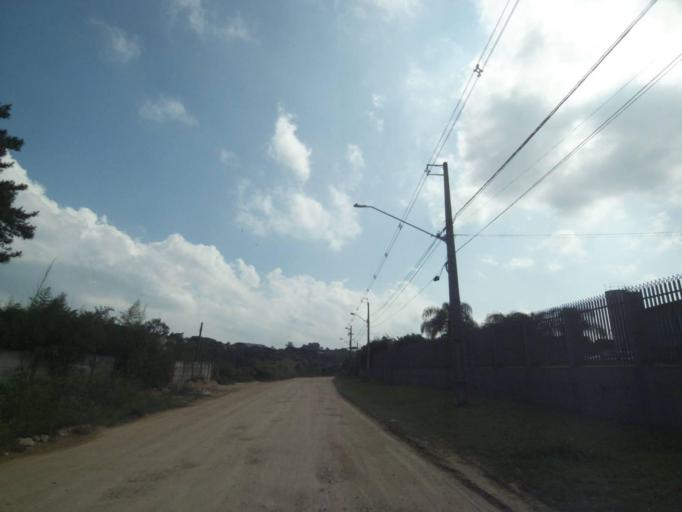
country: BR
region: Parana
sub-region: Araucaria
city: Araucaria
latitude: -25.5139
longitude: -49.3428
